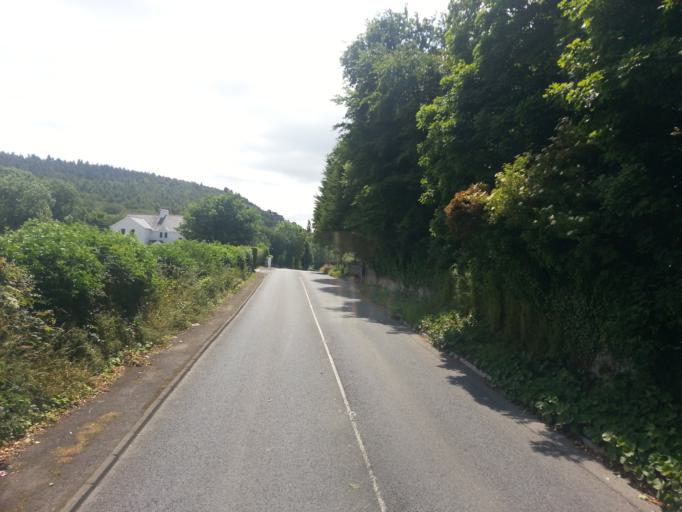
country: IE
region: Leinster
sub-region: Wicklow
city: Enniskerry
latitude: 53.2247
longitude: -6.1822
